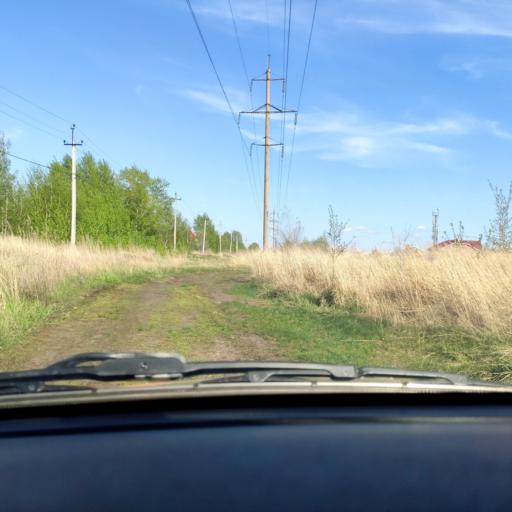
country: RU
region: Samara
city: Tol'yatti
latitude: 53.5610
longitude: 49.3755
